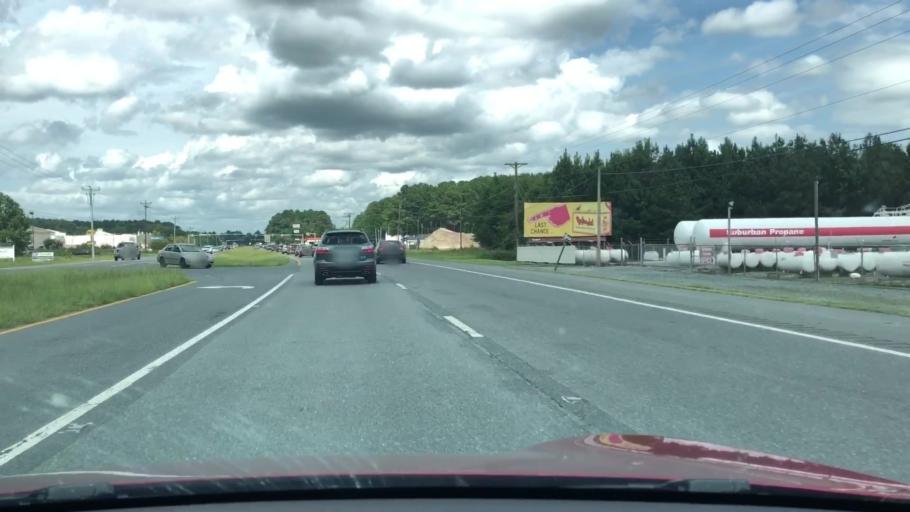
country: US
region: Virginia
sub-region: Accomack County
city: Onancock
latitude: 37.6805
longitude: -75.7229
